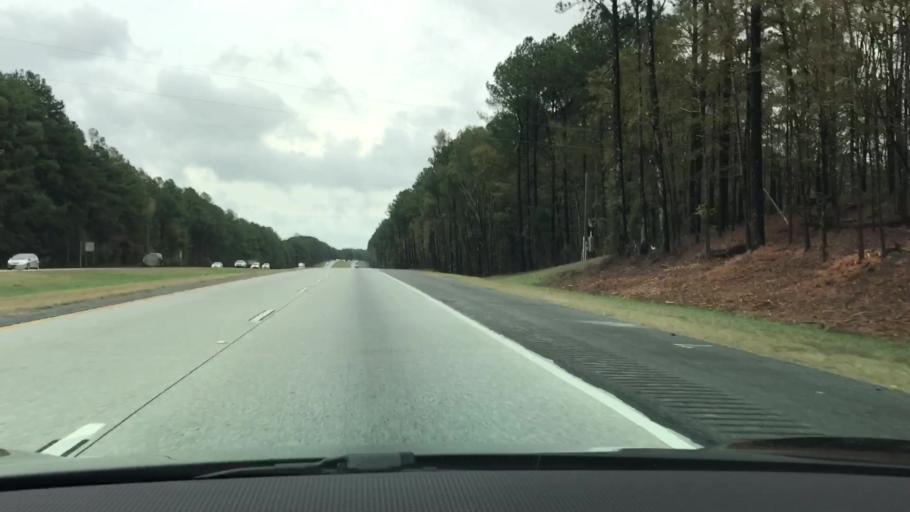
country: US
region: Georgia
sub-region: Taliaferro County
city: Crawfordville
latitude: 33.5268
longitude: -82.8902
